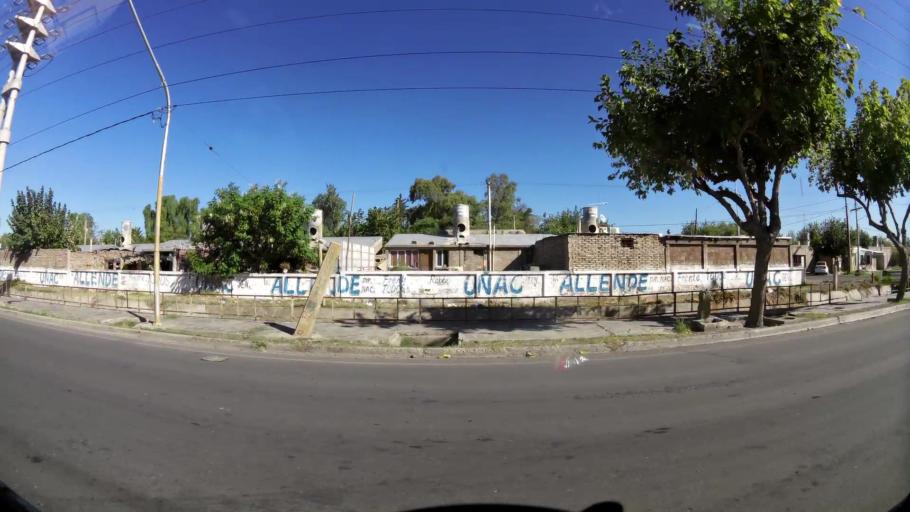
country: AR
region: San Juan
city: Villa Paula de Sarmiento
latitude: -31.5091
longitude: -68.5249
